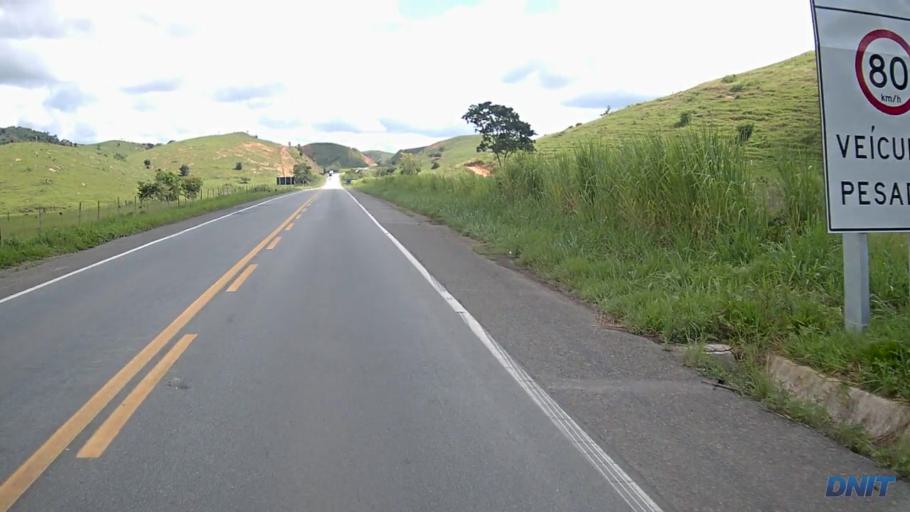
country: BR
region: Minas Gerais
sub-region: Belo Oriente
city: Belo Oriente
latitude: -19.1333
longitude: -42.2132
